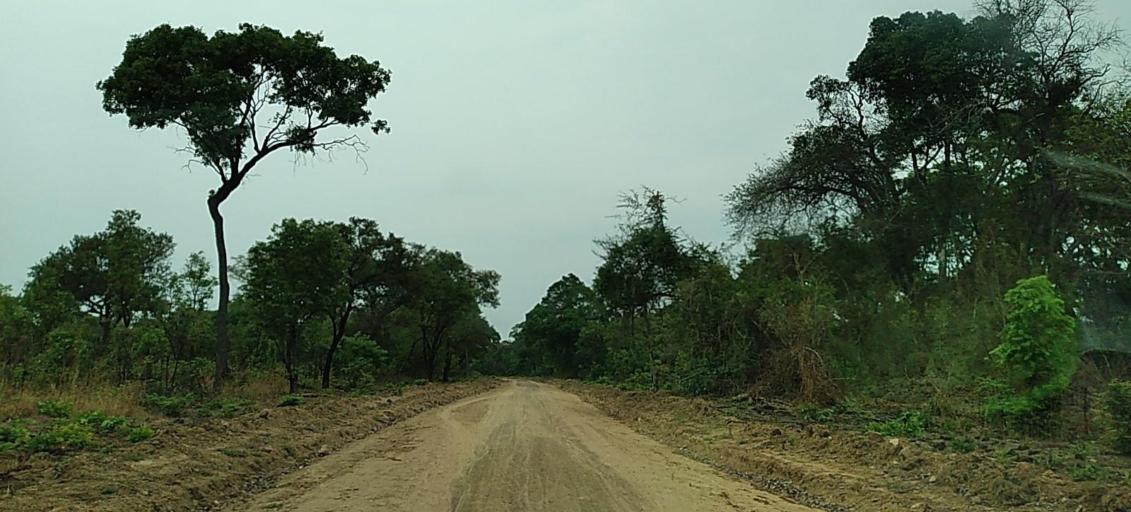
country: ZM
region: North-Western
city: Solwezi
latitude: -12.5174
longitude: 26.5256
